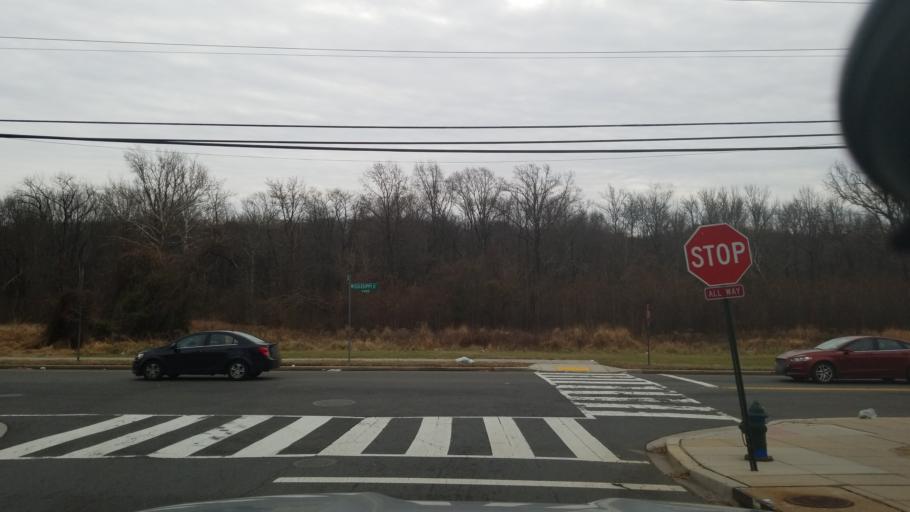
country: US
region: Maryland
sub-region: Prince George's County
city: Hillcrest Heights
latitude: 38.8418
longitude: -76.9827
